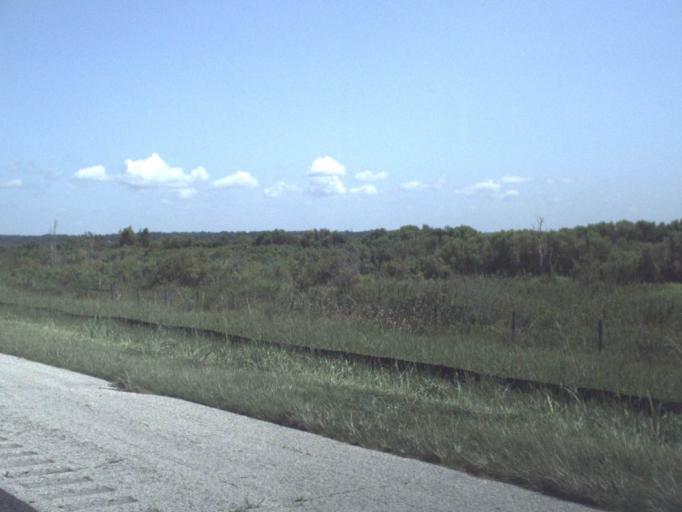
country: US
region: Florida
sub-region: Alachua County
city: Gainesville
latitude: 29.5615
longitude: -82.3461
